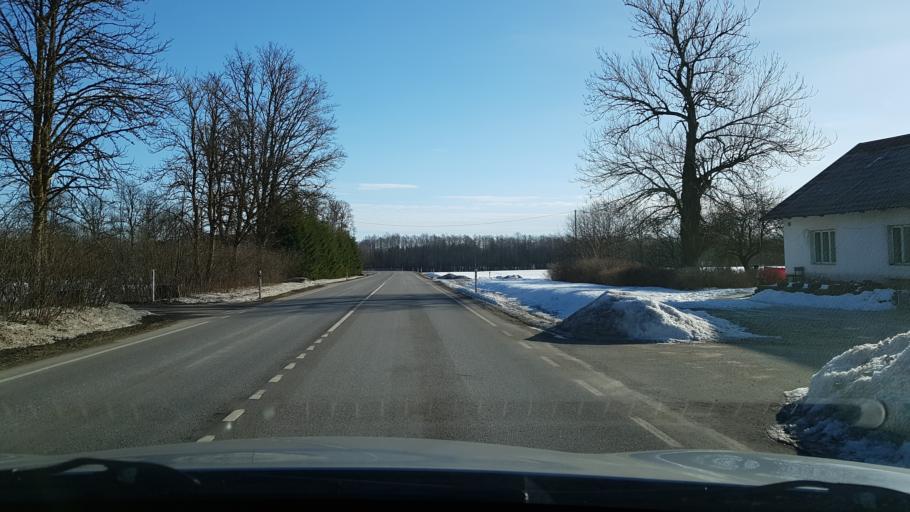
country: EE
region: Viljandimaa
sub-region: Vohma linn
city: Vohma
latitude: 58.6378
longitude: 25.6827
